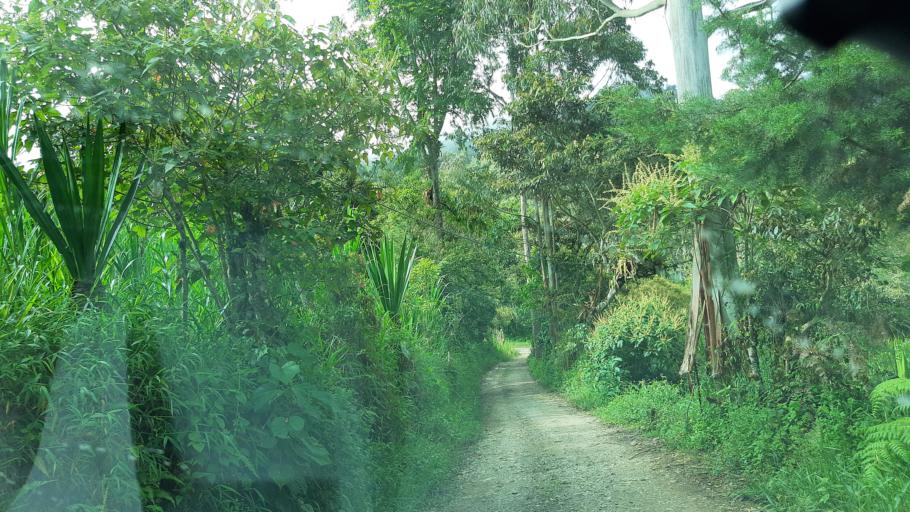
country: CO
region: Boyaca
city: Garagoa
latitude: 5.0405
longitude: -73.3451
